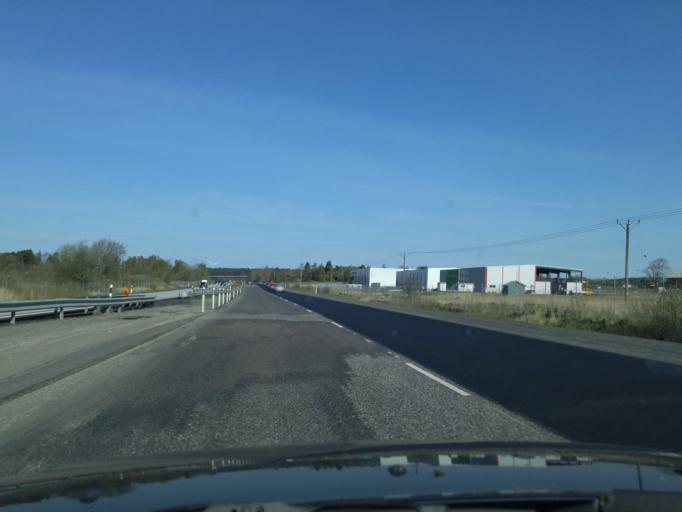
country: SE
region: Vaestra Goetaland
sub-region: Kungalvs Kommun
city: Kungalv
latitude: 57.8943
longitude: 11.9316
